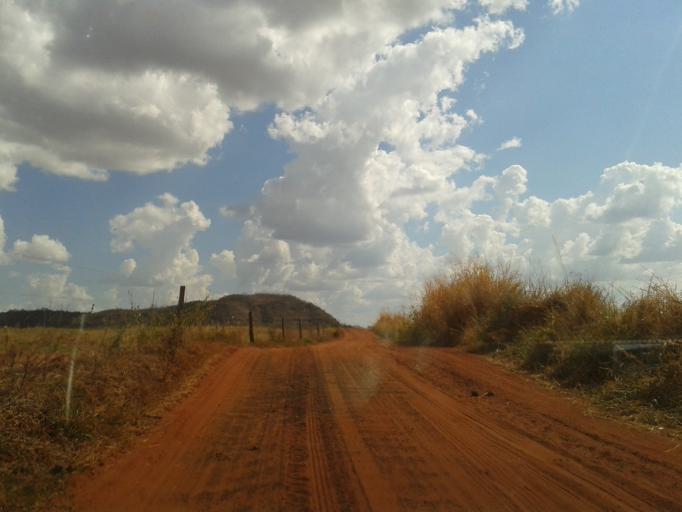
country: BR
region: Minas Gerais
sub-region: Santa Vitoria
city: Santa Vitoria
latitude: -19.1978
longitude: -49.9279
